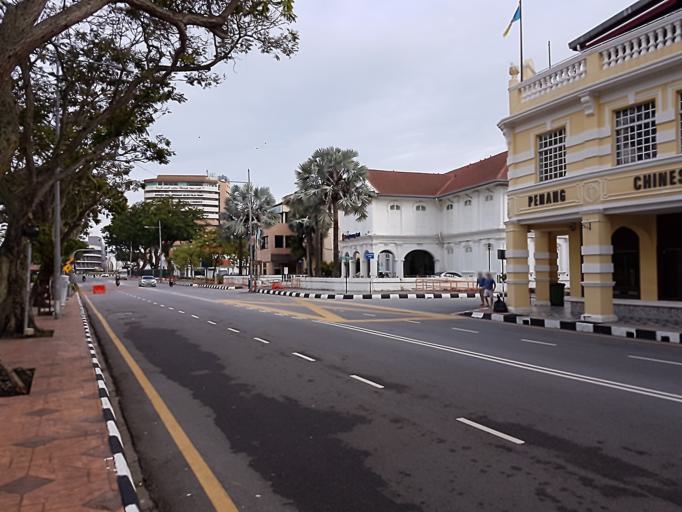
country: MY
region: Penang
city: George Town
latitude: 5.4202
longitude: 100.3418
